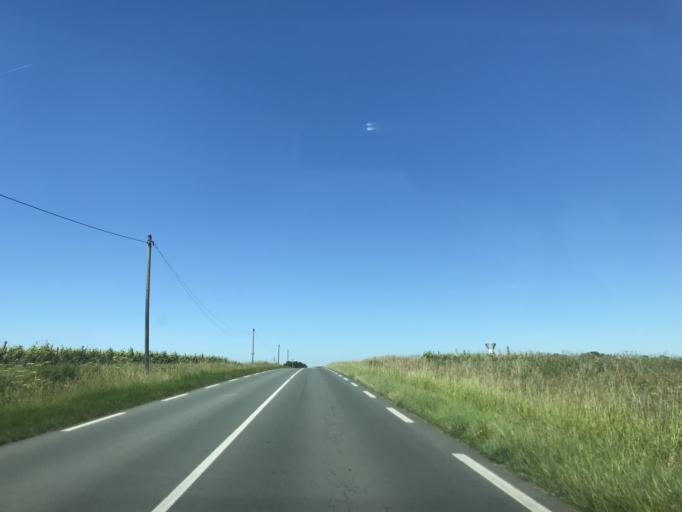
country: FR
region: Poitou-Charentes
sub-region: Departement de la Charente-Maritime
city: Perignac
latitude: 45.5778
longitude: -0.4515
